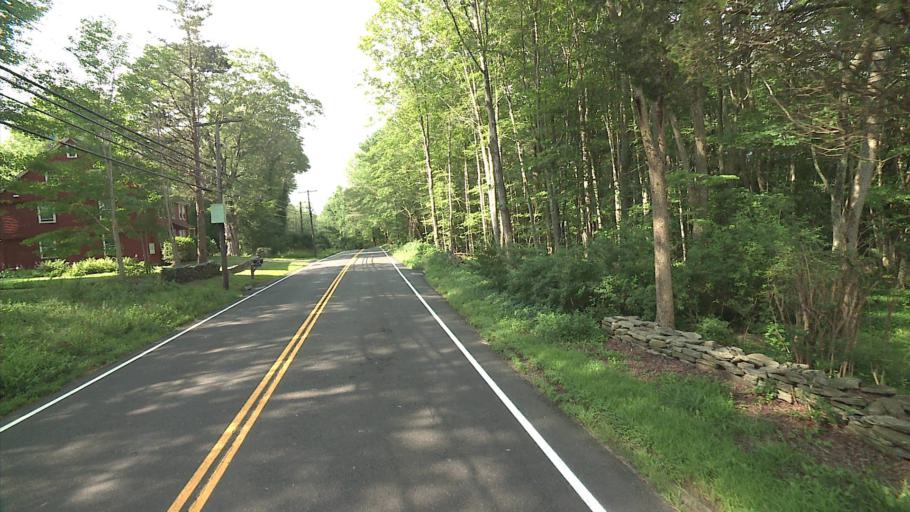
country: US
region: Connecticut
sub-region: New Haven County
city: Madison
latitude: 41.3845
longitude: -72.5649
